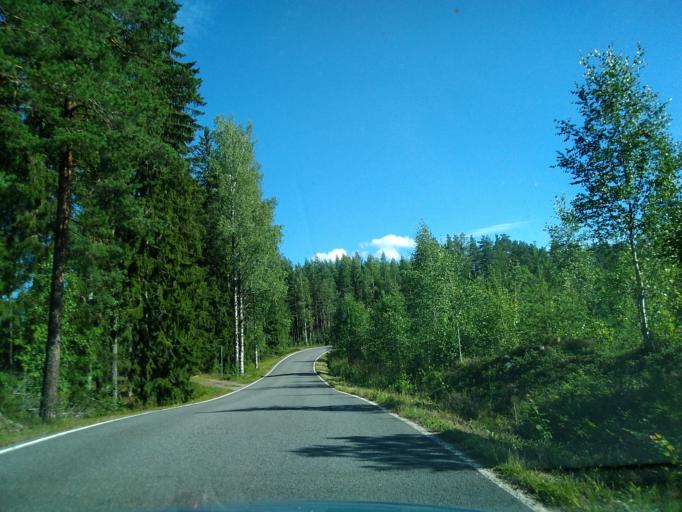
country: FI
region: Uusimaa
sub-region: Helsinki
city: Kaerkoelae
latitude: 60.7767
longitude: 24.0713
